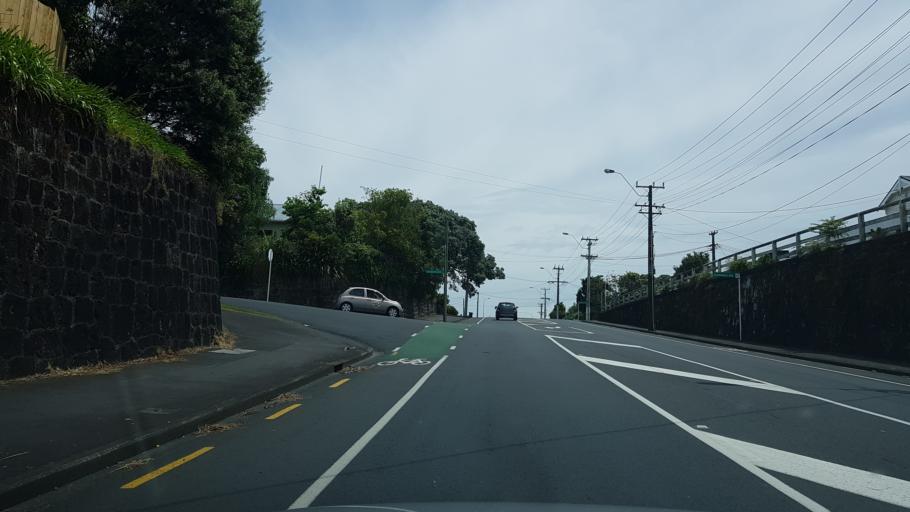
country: NZ
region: Auckland
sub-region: Auckland
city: North Shore
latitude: -36.8151
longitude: 174.7933
